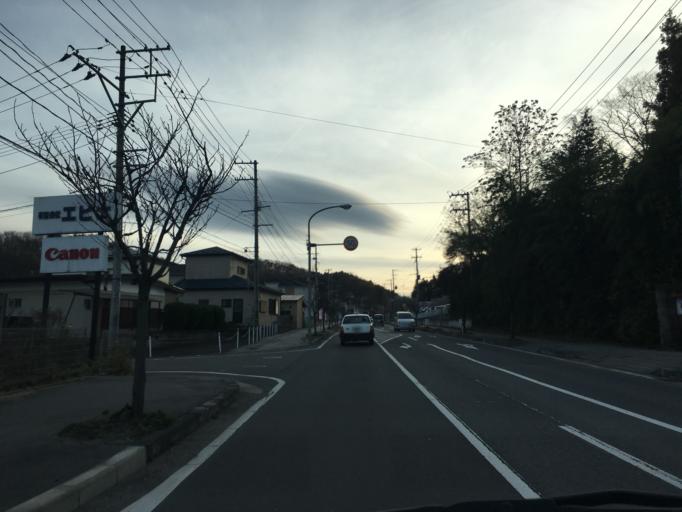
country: JP
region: Fukushima
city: Ishikawa
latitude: 37.1169
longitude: 140.2281
